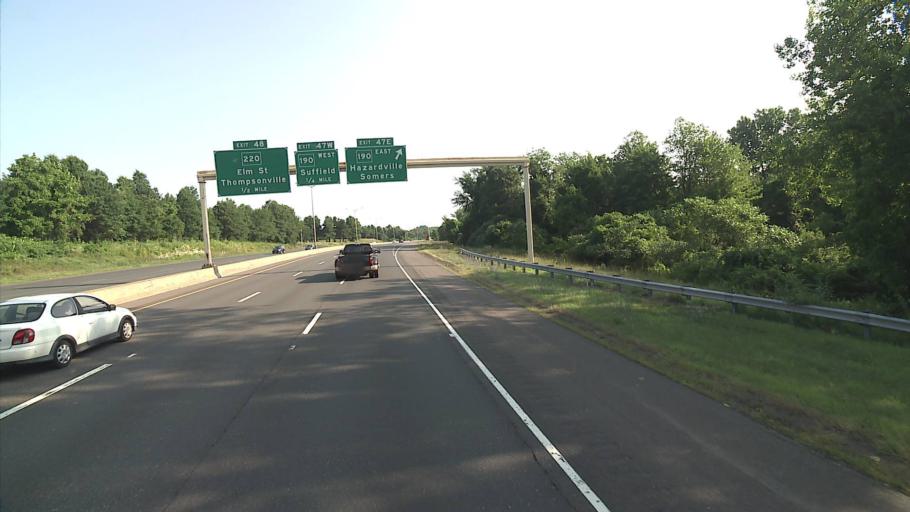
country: US
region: Connecticut
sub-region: Hartford County
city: Enfield
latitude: 41.9852
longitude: -72.5884
